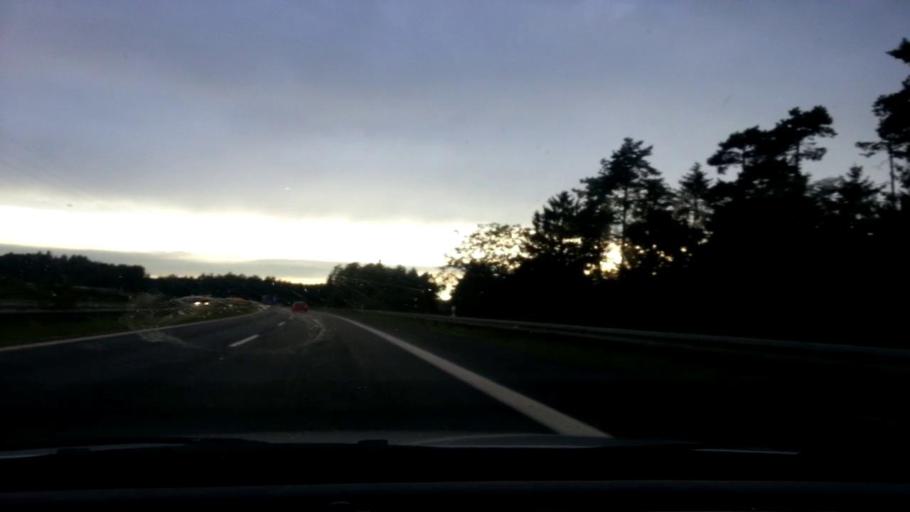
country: DE
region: Bavaria
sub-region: Upper Franconia
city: Stadelhofen
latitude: 50.0103
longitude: 11.2328
